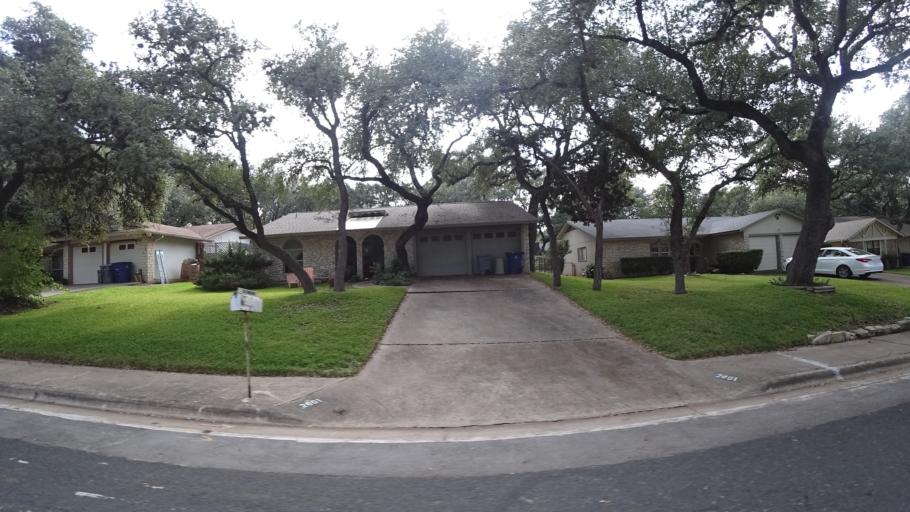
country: US
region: Texas
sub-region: Travis County
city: Shady Hollow
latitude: 30.2011
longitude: -97.8162
